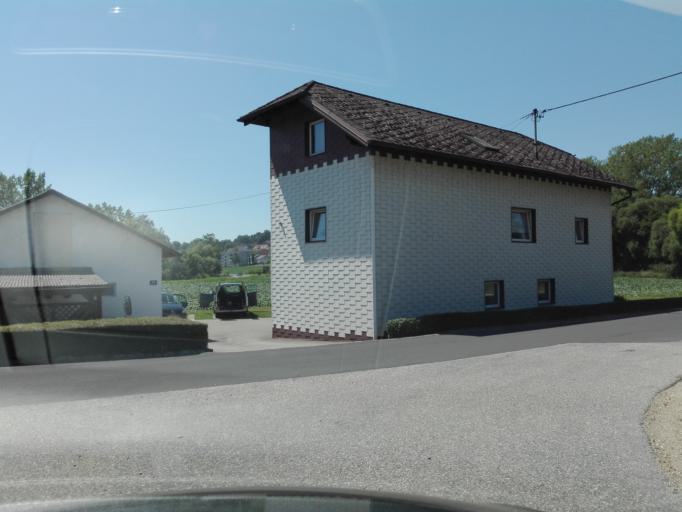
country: AT
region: Upper Austria
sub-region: Politischer Bezirk Urfahr-Umgebung
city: Engerwitzdorf
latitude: 48.2829
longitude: 14.4459
